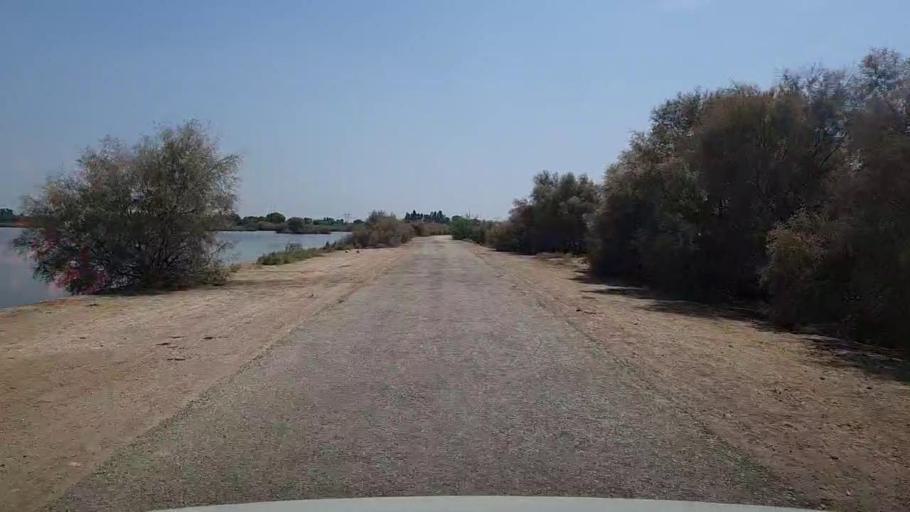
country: PK
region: Sindh
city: Kandhkot
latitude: 28.2970
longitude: 69.3520
